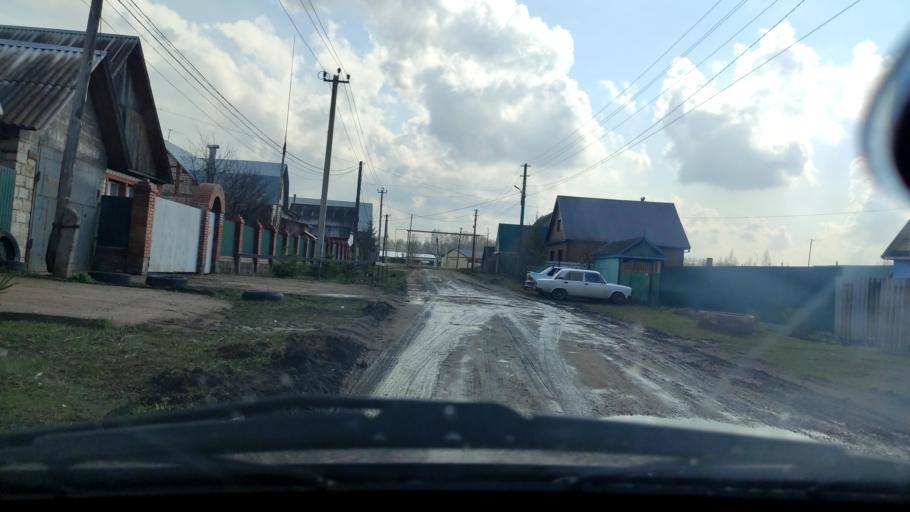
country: RU
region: Bashkortostan
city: Iglino
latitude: 54.8199
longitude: 56.3736
